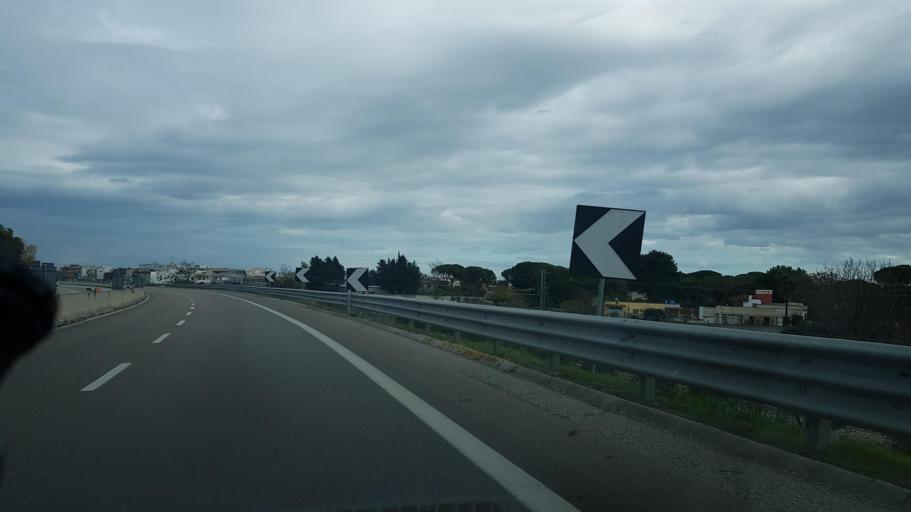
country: IT
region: Apulia
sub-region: Provincia di Brindisi
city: Latiano
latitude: 40.5488
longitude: 17.7057
